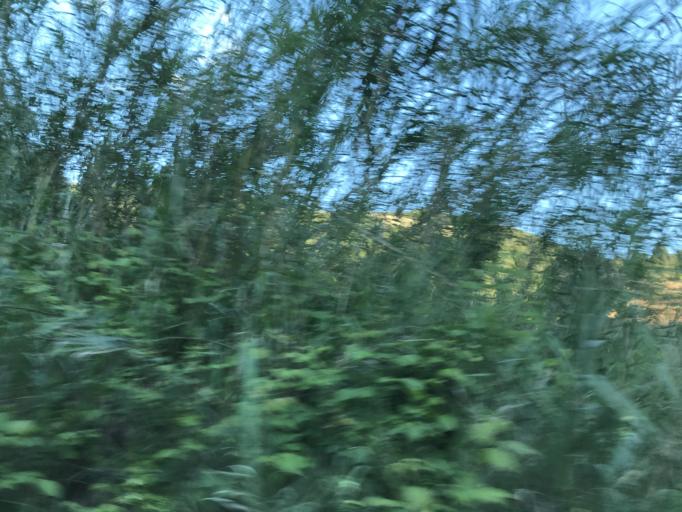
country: TR
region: Hatay
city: Buyukcat
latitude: 36.0872
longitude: 36.0527
